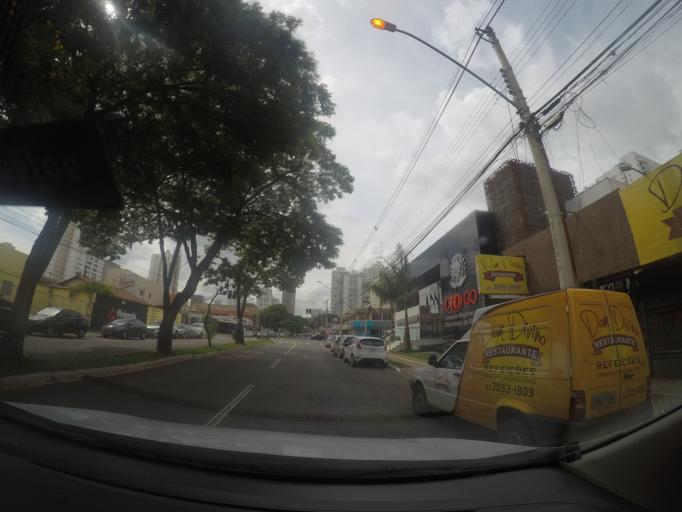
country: BR
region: Goias
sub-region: Goiania
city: Goiania
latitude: -16.6956
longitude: -49.2783
